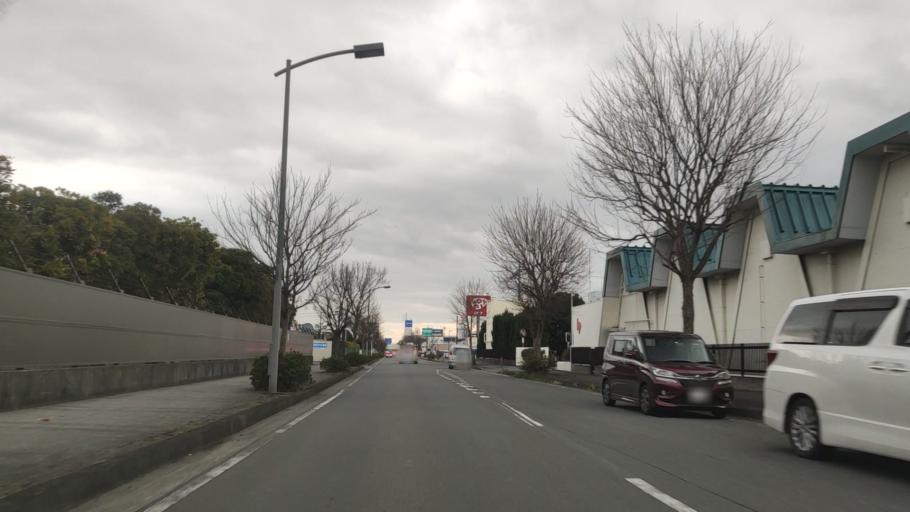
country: JP
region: Kanagawa
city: Odawara
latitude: 35.2887
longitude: 139.1893
